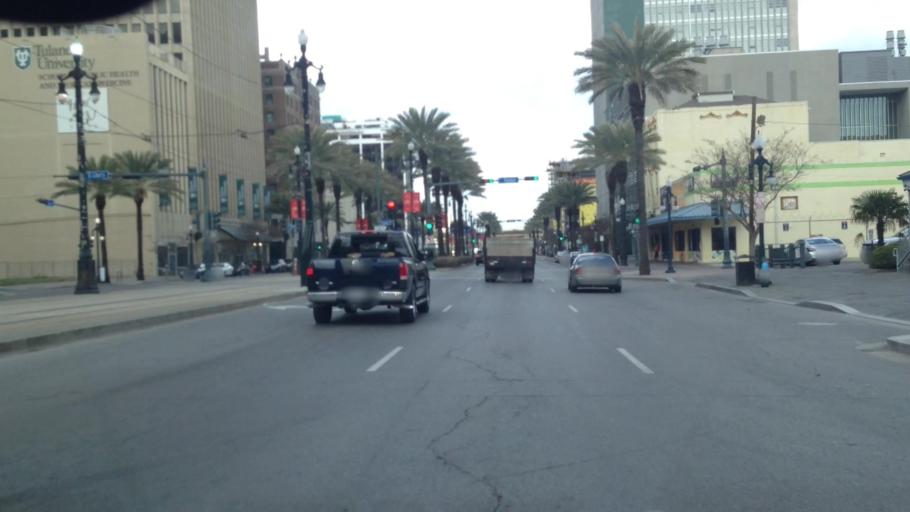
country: US
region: Louisiana
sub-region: Orleans Parish
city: New Orleans
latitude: 29.9566
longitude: -90.0740
